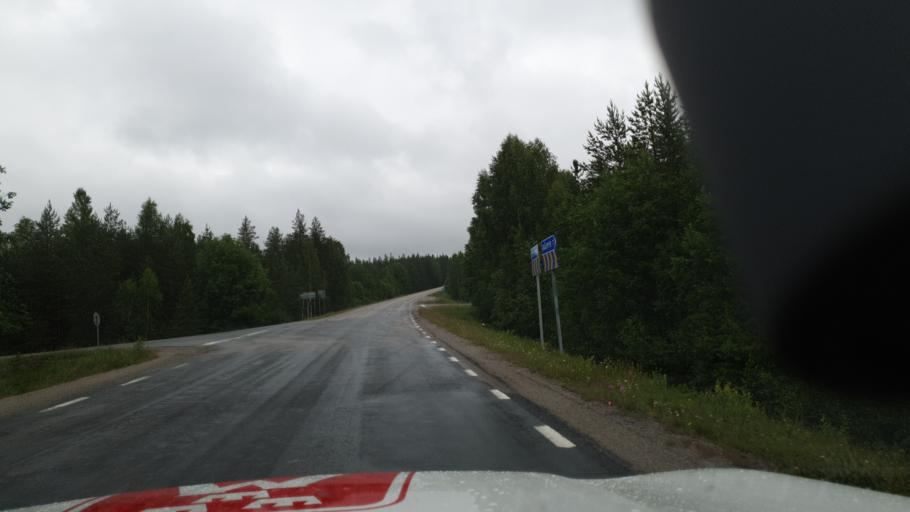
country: SE
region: Vaesterbotten
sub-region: Vannas Kommun
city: Vaennaes
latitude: 63.7855
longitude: 19.7452
